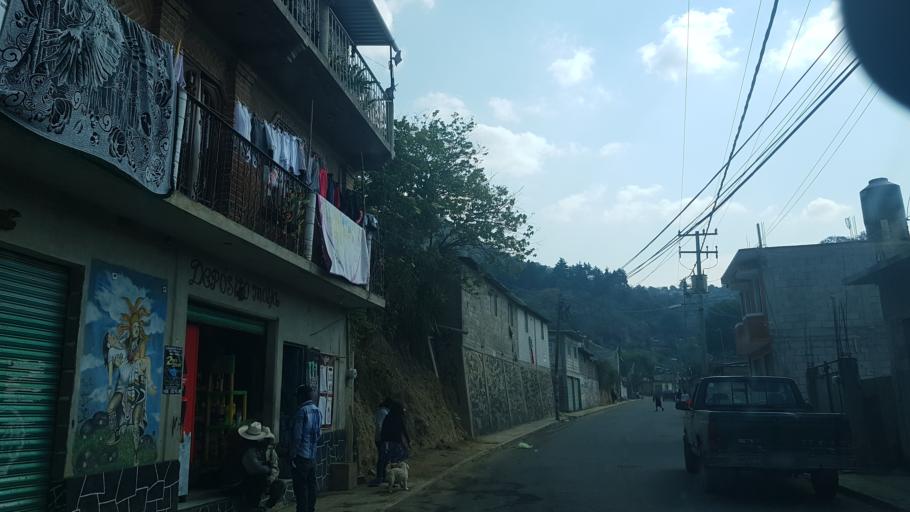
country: MX
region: Puebla
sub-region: Tochimilco
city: San Antonio Alpanocan
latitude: 18.8770
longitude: -98.7076
